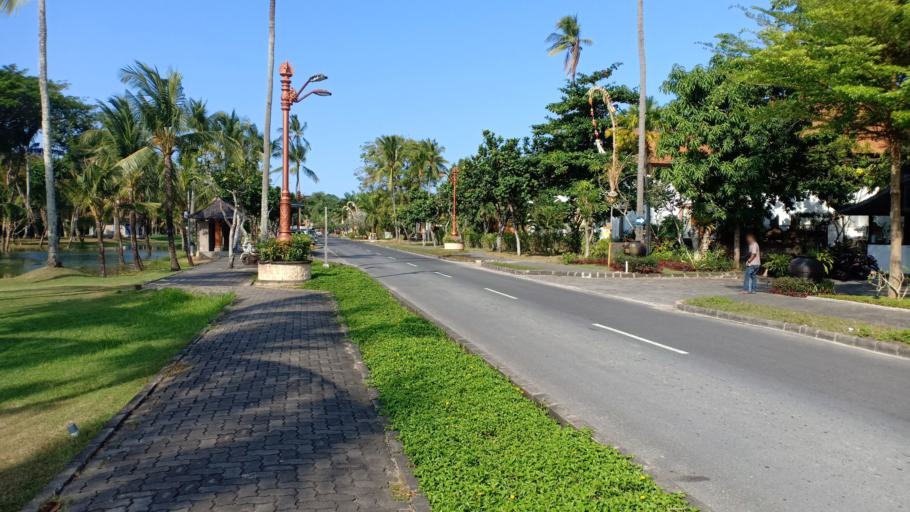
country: ID
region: Bali
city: Bualu
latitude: -8.8009
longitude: 115.2311
